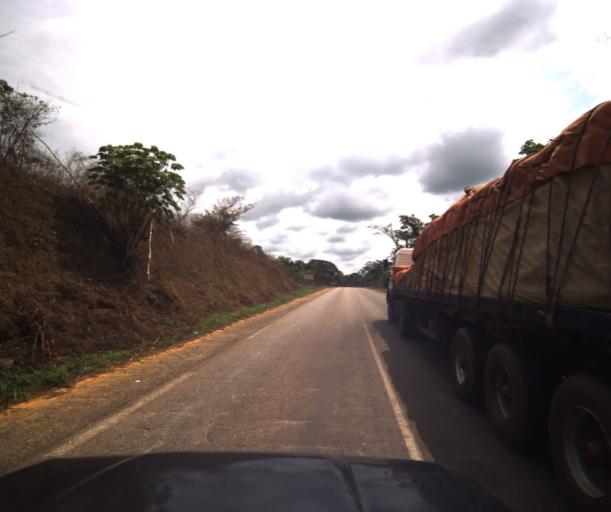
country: CM
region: Littoral
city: Edea
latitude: 3.8458
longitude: 10.4743
